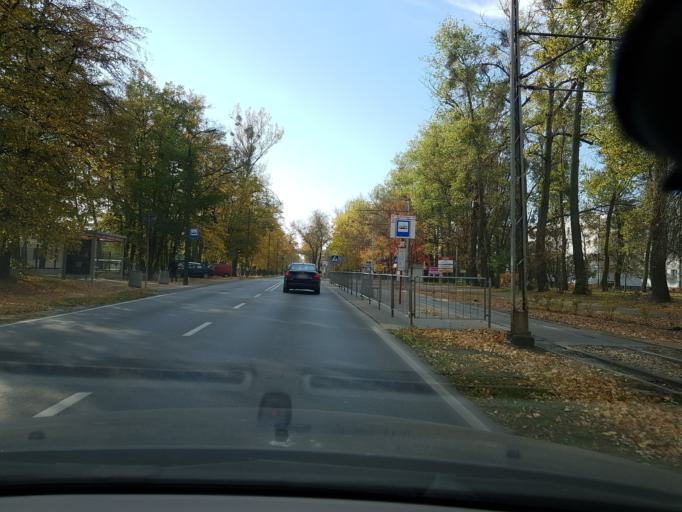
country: PL
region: Masovian Voivodeship
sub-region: Warszawa
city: Bemowo
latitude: 52.2567
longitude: 20.8978
